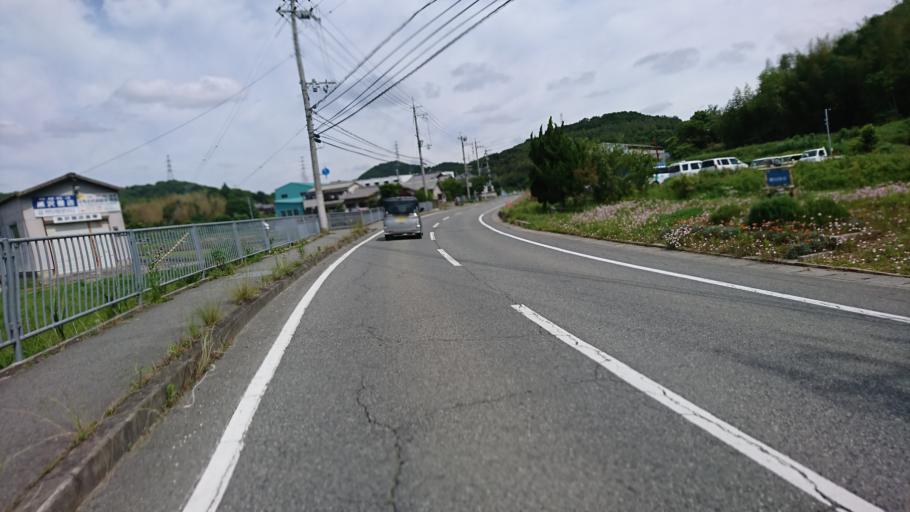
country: JP
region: Hyogo
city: Shirahamacho-usazakiminami
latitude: 34.7939
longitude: 134.7475
